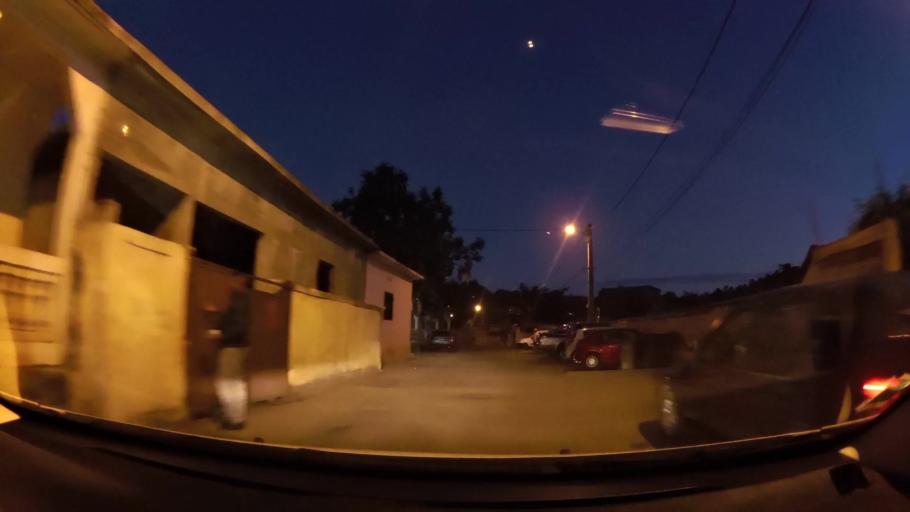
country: YT
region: Bandraboua
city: Bandraboua
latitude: -12.7217
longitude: 45.1204
